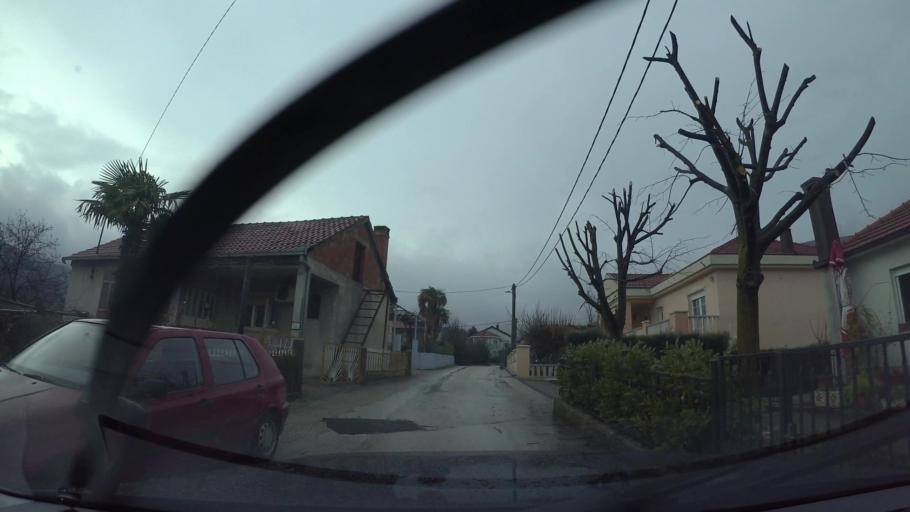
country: BA
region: Federation of Bosnia and Herzegovina
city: Cim
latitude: 43.3480
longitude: 17.7775
